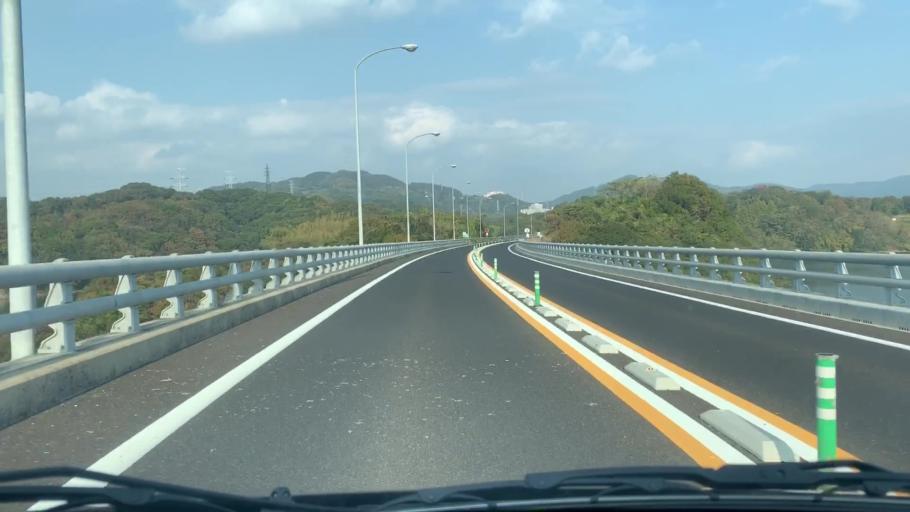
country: JP
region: Nagasaki
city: Sasebo
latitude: 33.0753
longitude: 129.7684
